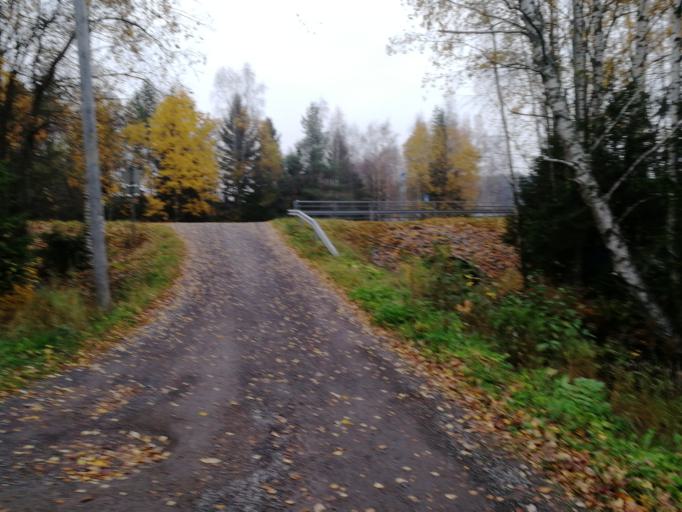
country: FI
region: Pirkanmaa
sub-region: Tampere
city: Tampere
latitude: 61.4528
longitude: 23.8891
